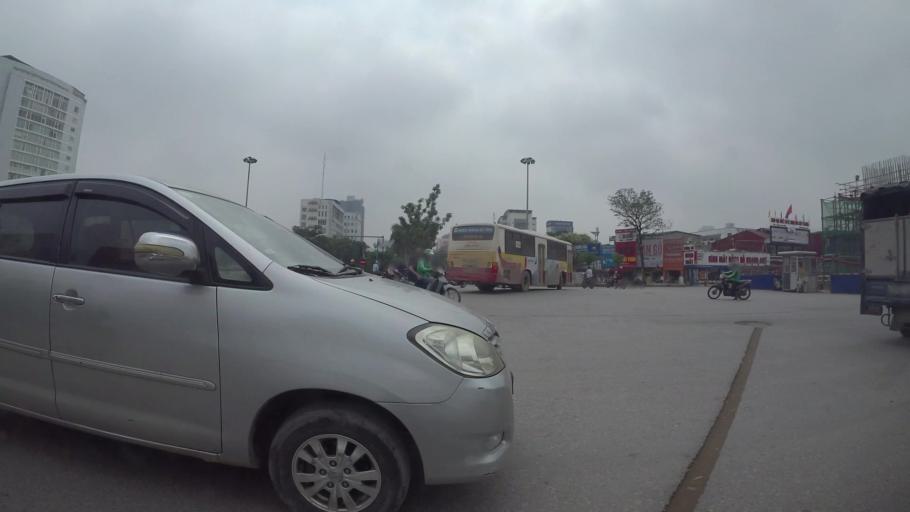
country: VN
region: Ha Noi
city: Cau Dien
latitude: 21.0460
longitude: 105.7811
